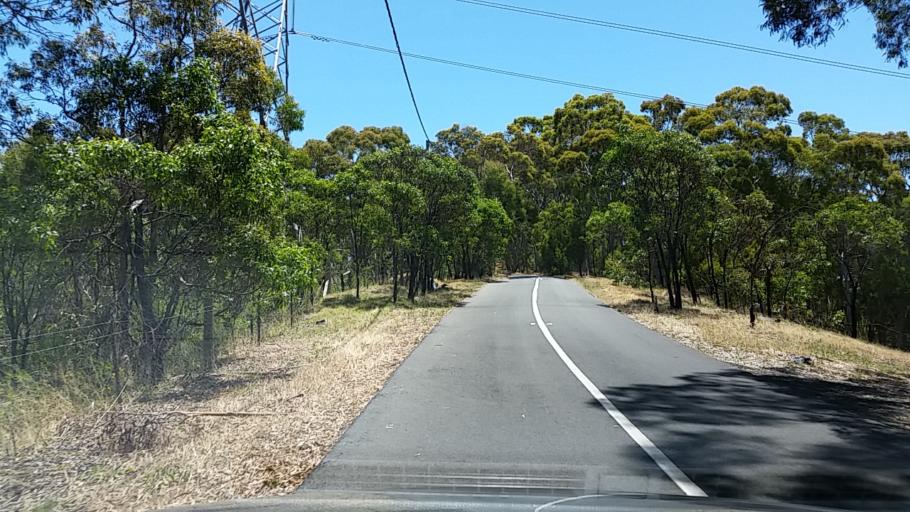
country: AU
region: South Australia
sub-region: Adelaide Hills
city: Upper Sturt
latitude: -34.9972
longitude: 138.6683
